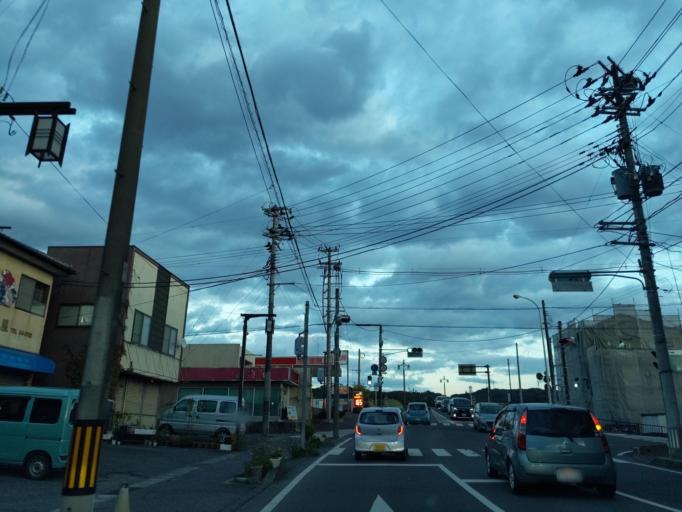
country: JP
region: Fukushima
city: Motomiya
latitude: 37.5183
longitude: 140.4044
